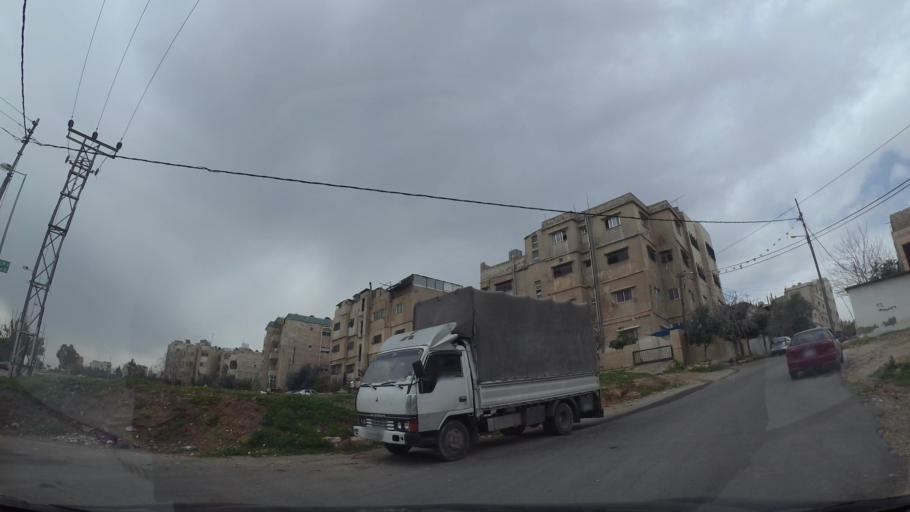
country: JO
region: Amman
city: Amman
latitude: 31.9764
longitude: 35.9334
